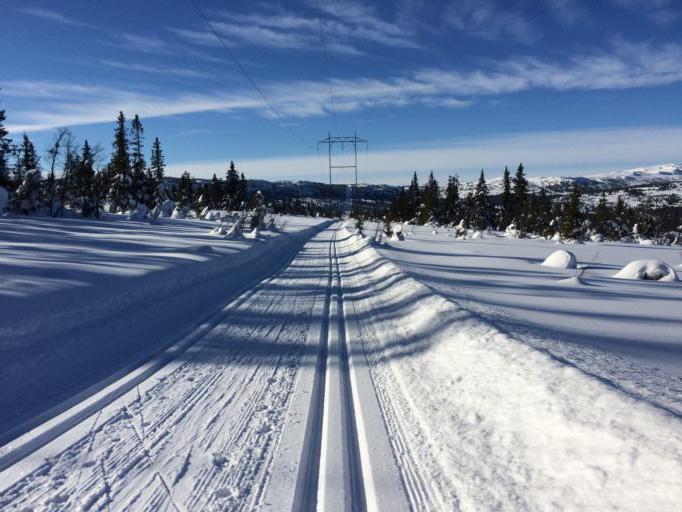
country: NO
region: Oppland
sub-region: Gausdal
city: Segalstad bru
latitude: 61.3153
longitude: 10.1019
